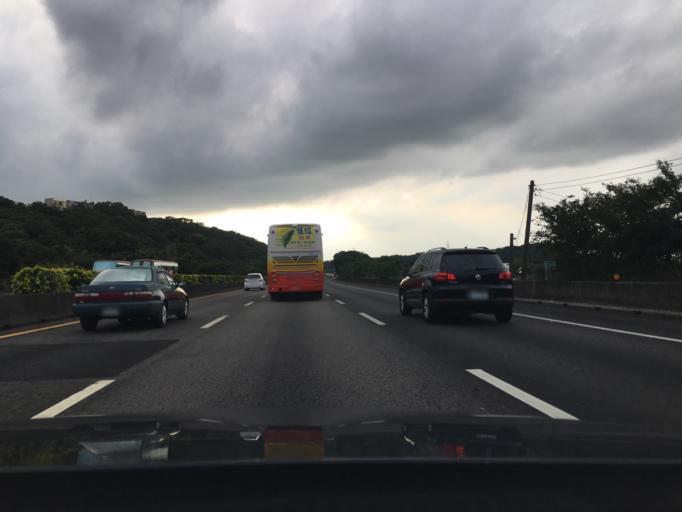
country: TW
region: Taiwan
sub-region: Hsinchu
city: Zhubei
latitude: 24.8931
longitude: 121.1203
